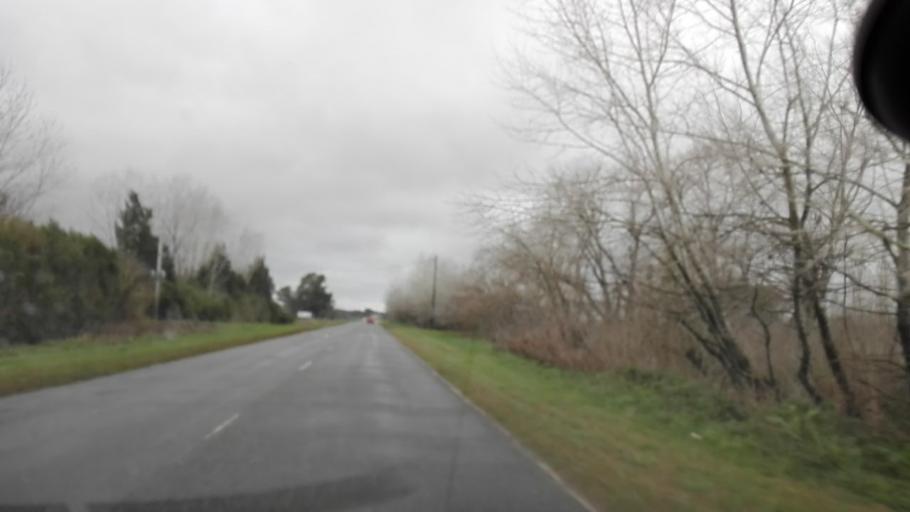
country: AR
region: Buenos Aires
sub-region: Partido de Brandsen
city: Brandsen
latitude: -35.1787
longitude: -58.2726
